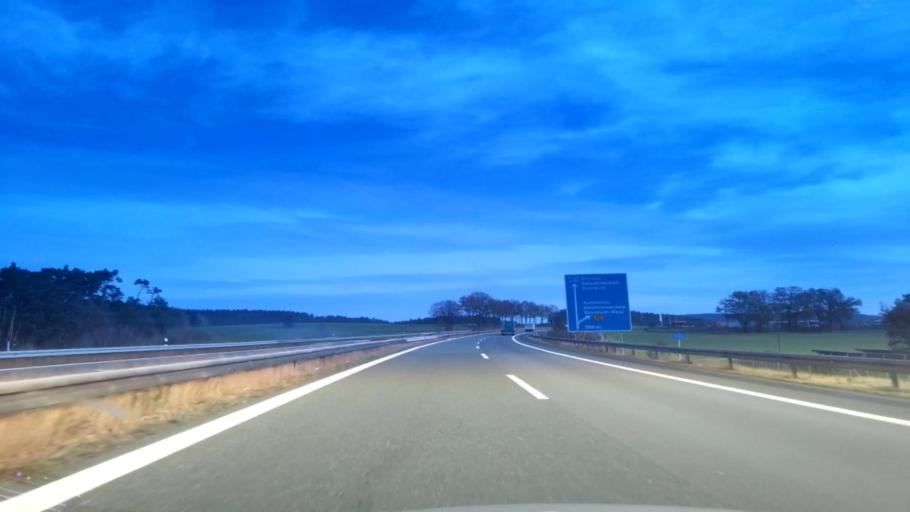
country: DE
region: Bavaria
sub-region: Upper Franconia
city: Neudrossenfeld
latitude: 50.0373
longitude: 11.4811
